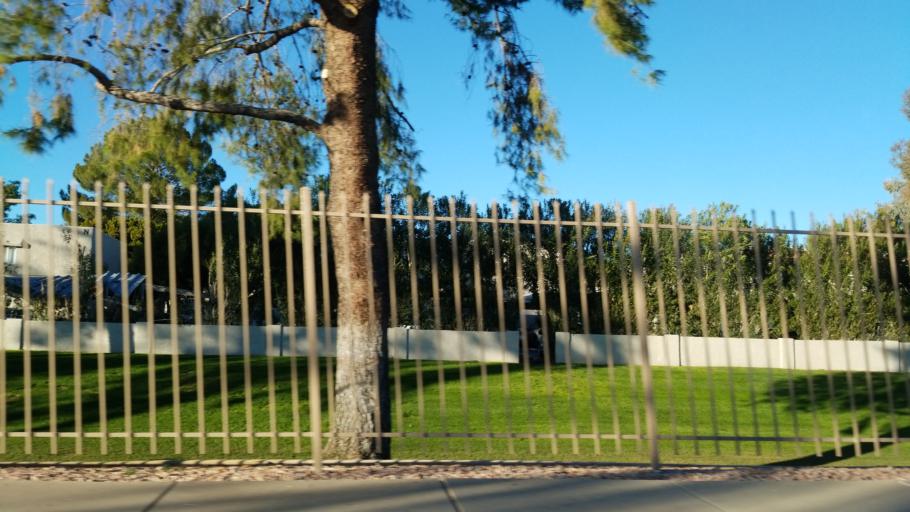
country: US
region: Arizona
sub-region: Maricopa County
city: Paradise Valley
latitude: 33.6051
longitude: -111.9851
